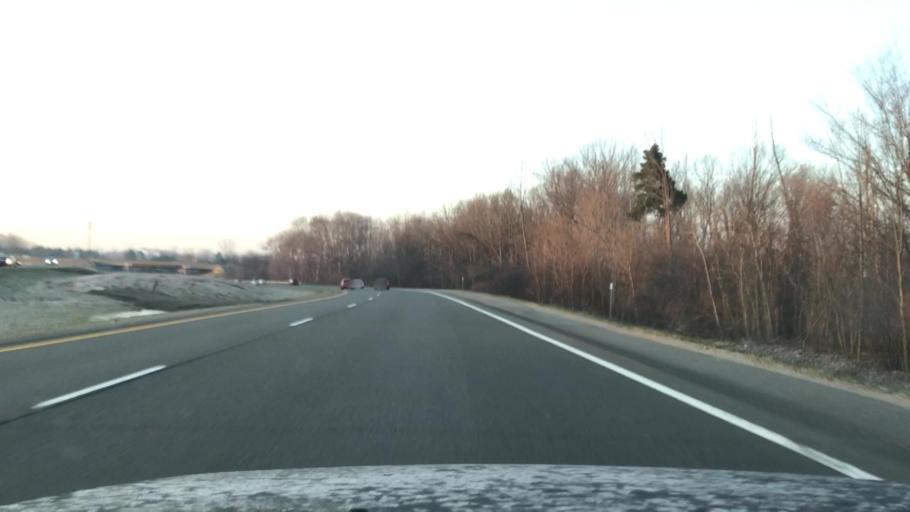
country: US
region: Michigan
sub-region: Kent County
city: East Grand Rapids
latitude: 42.9804
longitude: -85.6052
